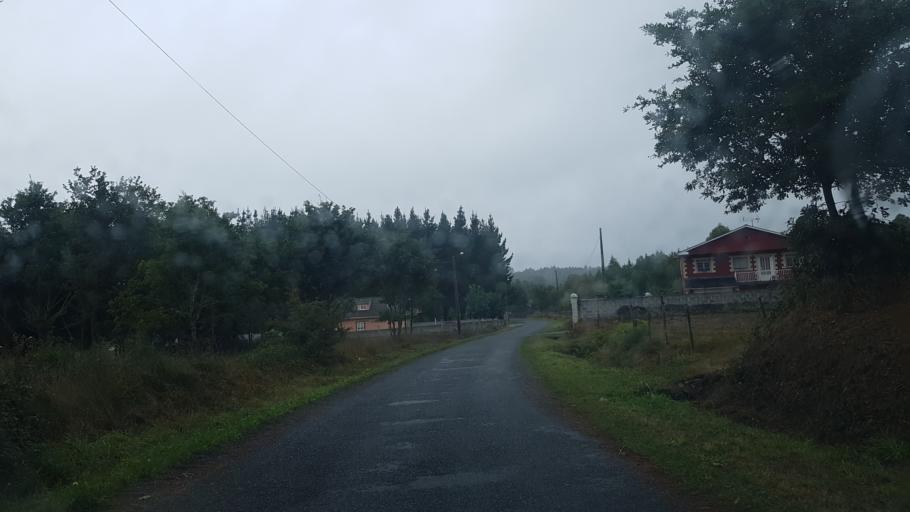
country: ES
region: Galicia
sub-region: Provincia de Lugo
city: Friol
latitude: 43.1171
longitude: -7.8160
